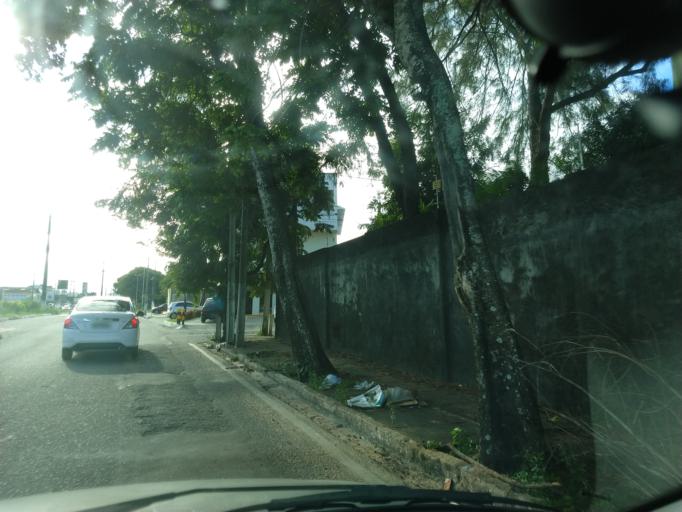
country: BR
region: Rio Grande do Norte
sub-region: Natal
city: Natal
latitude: -5.8436
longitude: -35.2188
